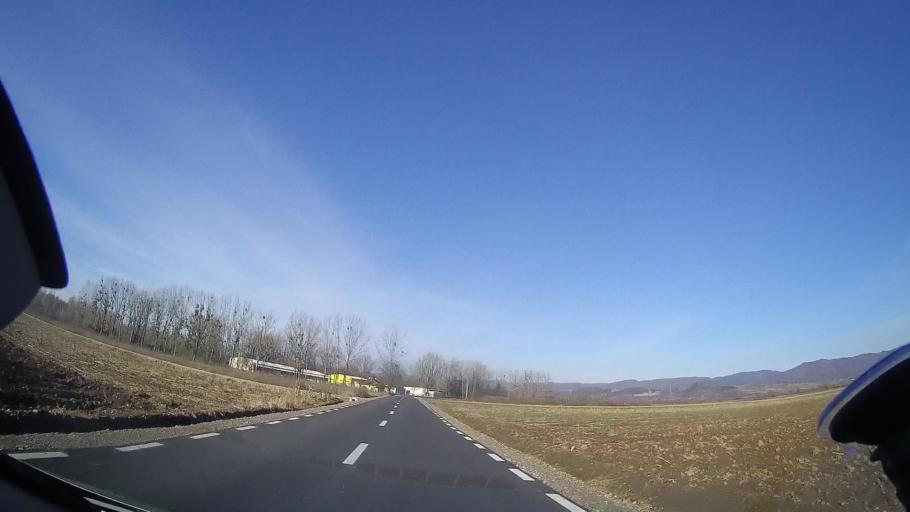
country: RO
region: Bihor
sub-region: Comuna Vadu Crisului
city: Vadu Crisului
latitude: 47.0026
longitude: 22.5024
